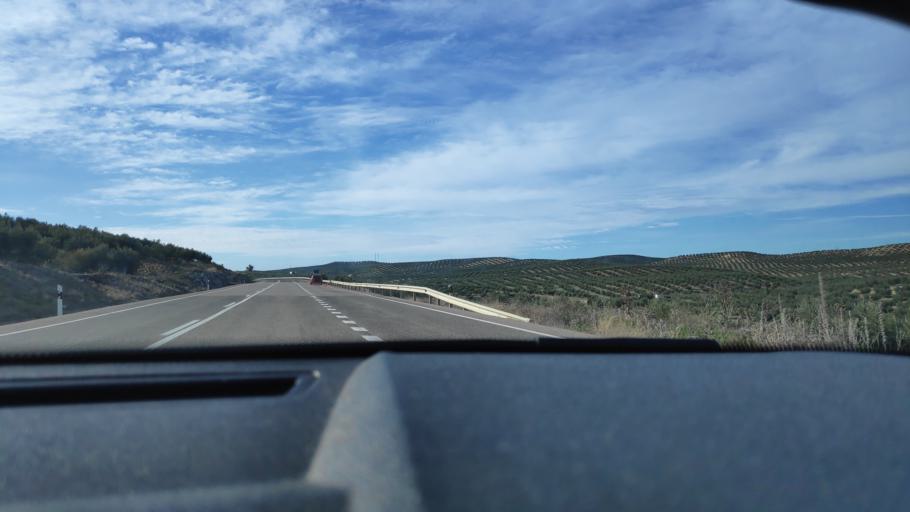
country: ES
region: Andalusia
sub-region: Provincia de Jaen
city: Porcuna
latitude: 37.8810
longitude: -4.2286
